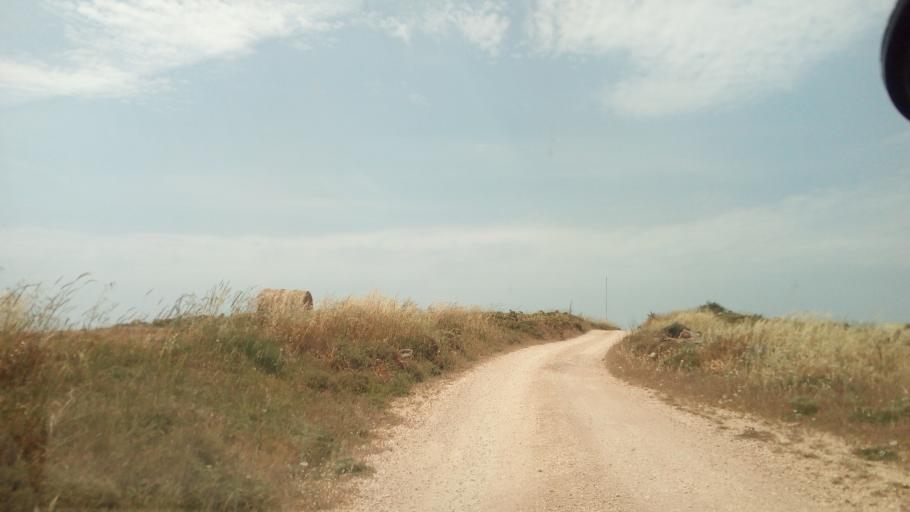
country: CY
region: Pafos
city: Polis
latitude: 34.9774
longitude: 32.3629
